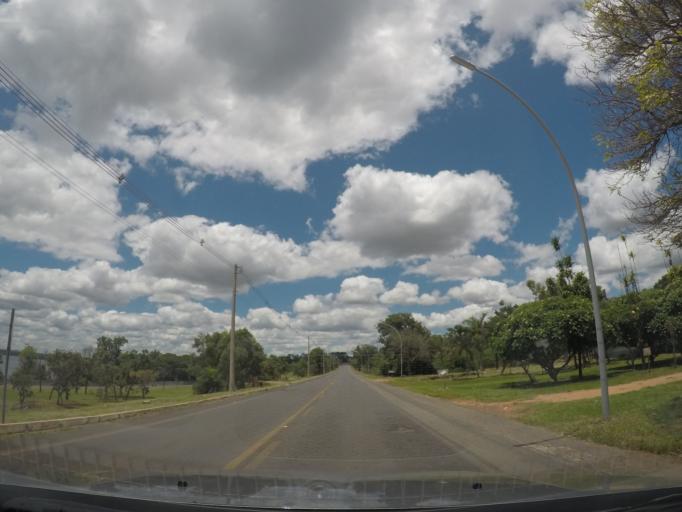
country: BR
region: Federal District
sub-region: Brasilia
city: Brasilia
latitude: -15.7799
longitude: -47.8087
